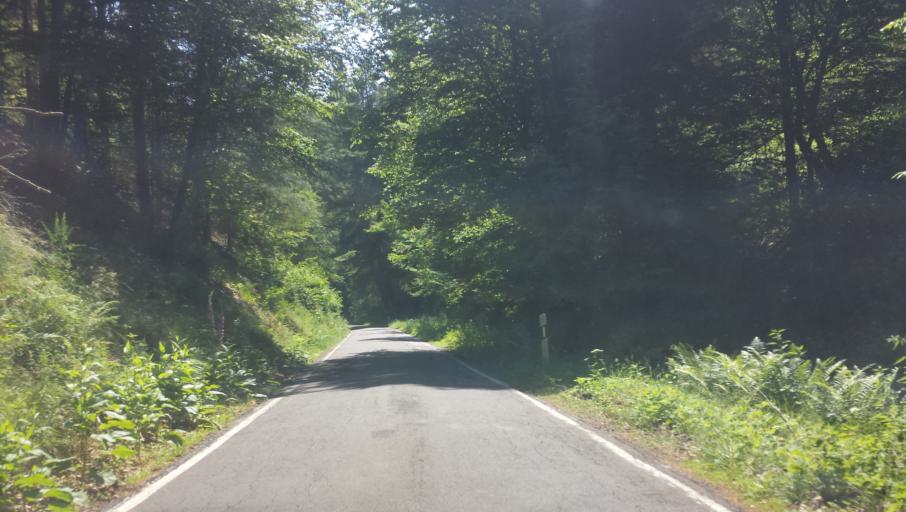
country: DE
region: Rheinland-Pfalz
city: Elmstein
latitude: 49.3670
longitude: 7.9210
